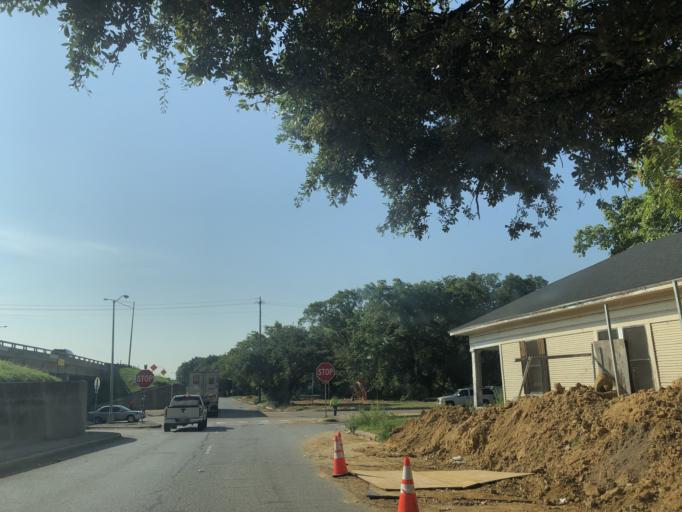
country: US
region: Texas
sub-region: Dallas County
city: Dallas
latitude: 32.7536
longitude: -96.7654
